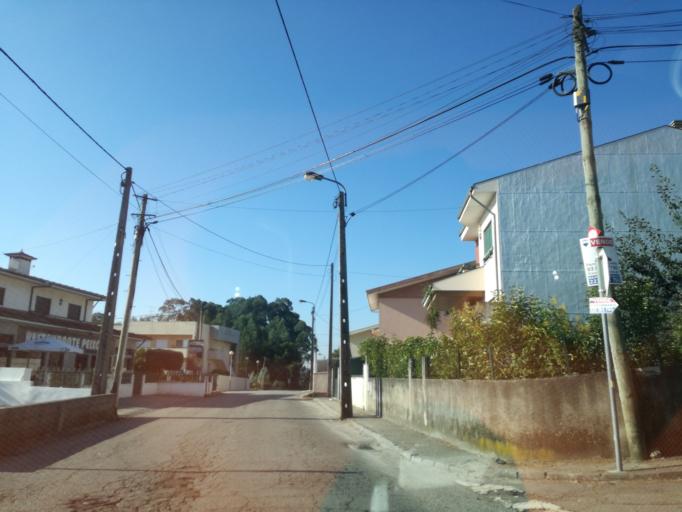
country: PT
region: Porto
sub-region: Maia
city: Nogueira
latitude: 41.2607
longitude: -8.5740
